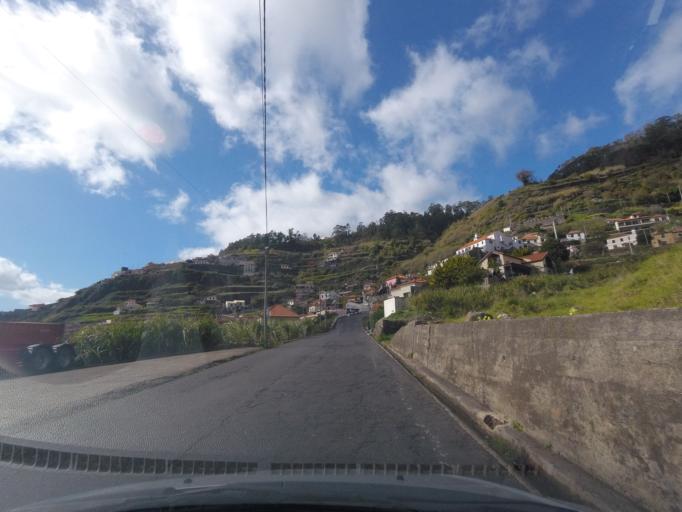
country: PT
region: Madeira
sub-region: Ribeira Brava
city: Campanario
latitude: 32.6608
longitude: -17.0102
